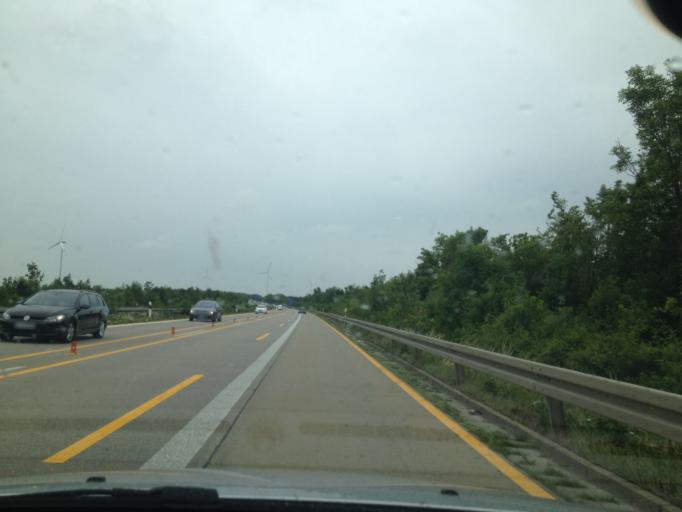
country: DE
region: Bavaria
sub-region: Regierungsbezirk Unterfranken
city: Biebelried
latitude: 49.7447
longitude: 10.1073
